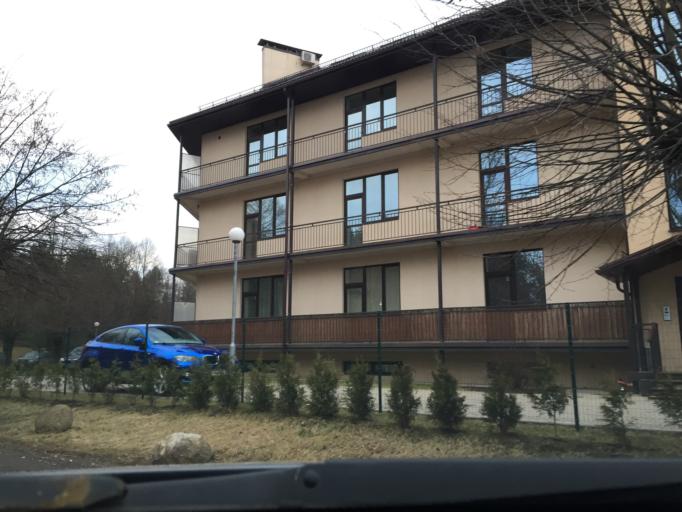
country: LV
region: Riga
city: Bergi
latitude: 56.9737
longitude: 24.2610
